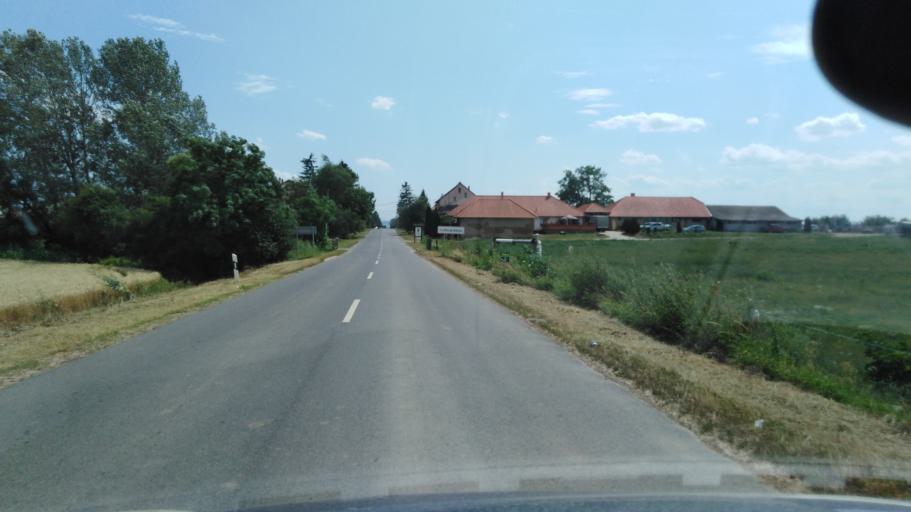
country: HU
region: Nograd
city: Szecseny
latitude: 48.1527
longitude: 19.5330
